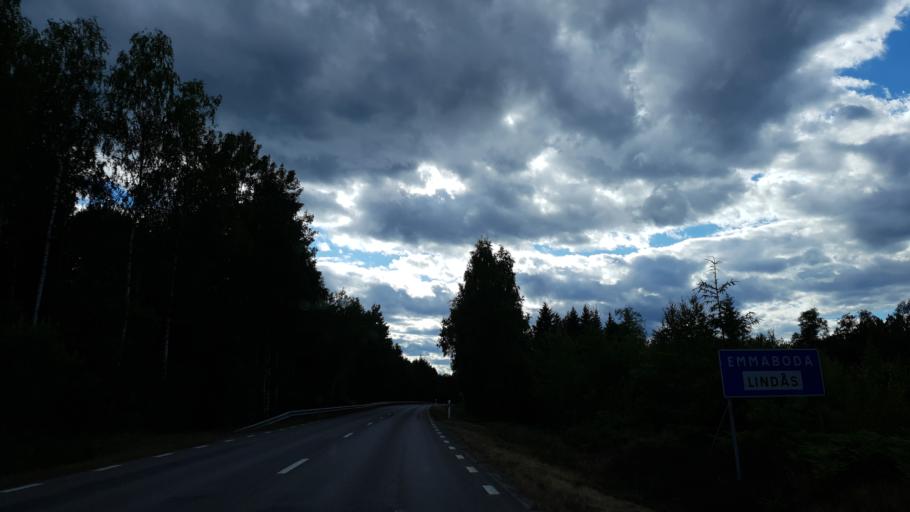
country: SE
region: Kalmar
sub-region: Emmaboda Kommun
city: Emmaboda
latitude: 56.6227
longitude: 15.5836
